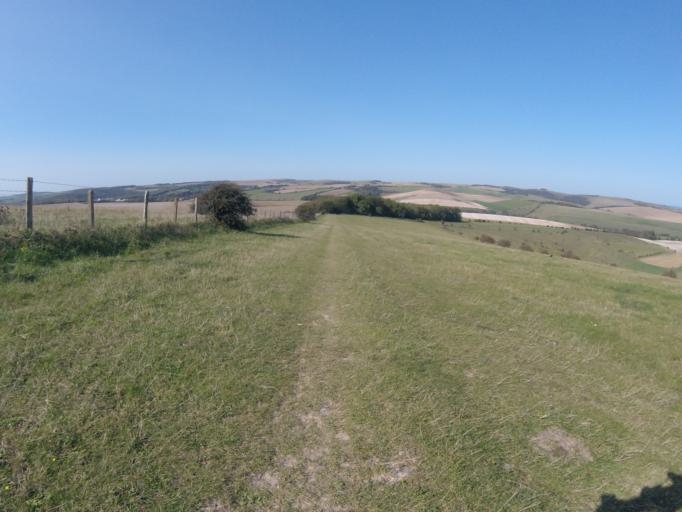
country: GB
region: England
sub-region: Brighton and Hove
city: Rottingdean
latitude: 50.8516
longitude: -0.0558
